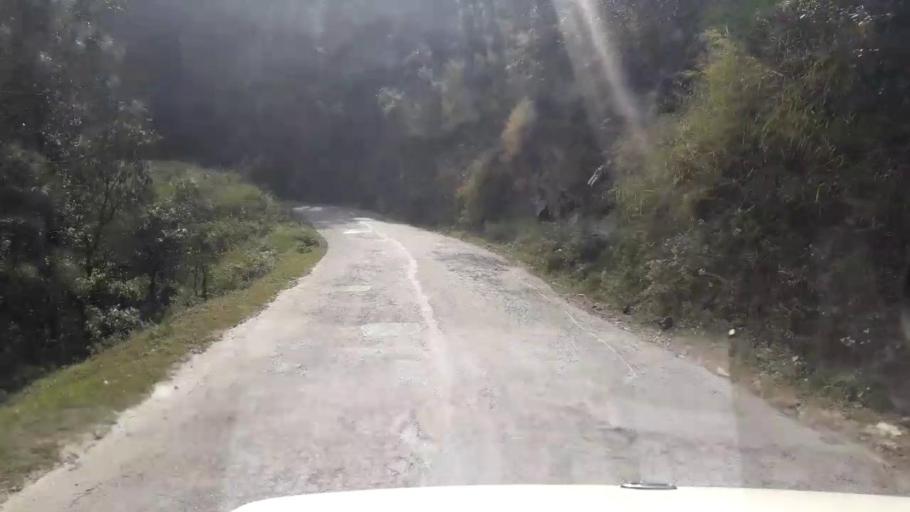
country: IN
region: Himachal Pradesh
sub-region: Shimla
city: Shimla
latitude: 31.0492
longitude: 77.1502
